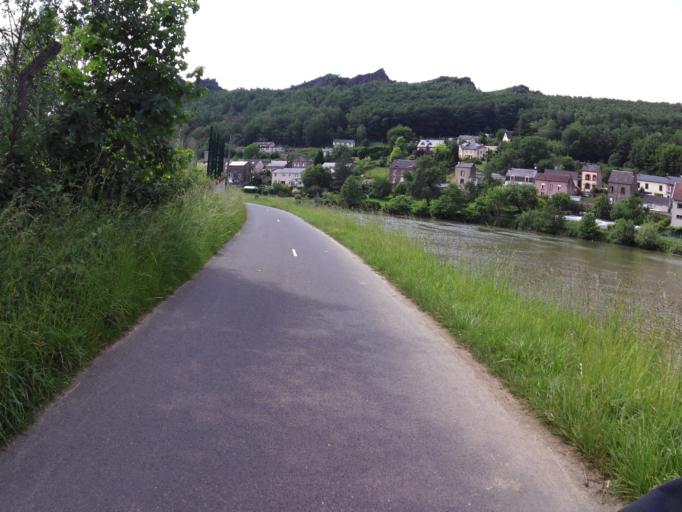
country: FR
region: Champagne-Ardenne
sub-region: Departement des Ardennes
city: Montherme
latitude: 49.8609
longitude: 4.7496
